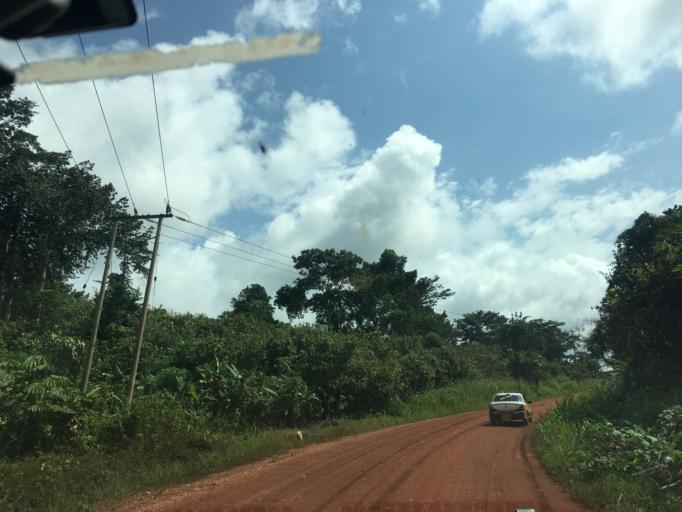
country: GH
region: Western
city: Wassa-Akropong
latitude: 5.7836
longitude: -2.3908
